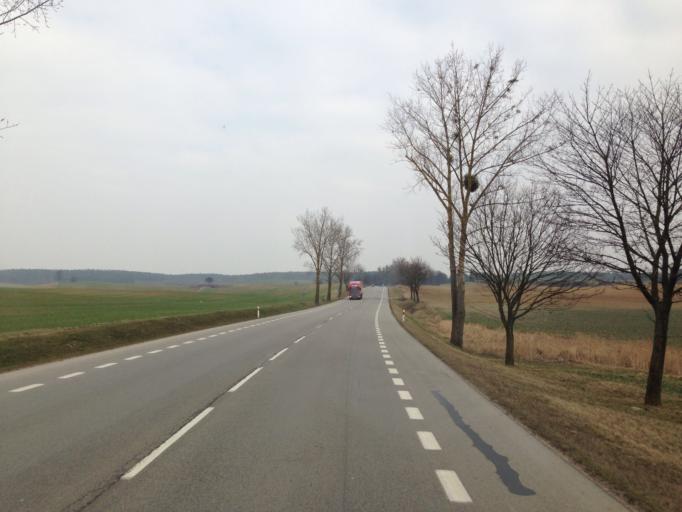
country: PL
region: Pomeranian Voivodeship
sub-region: Powiat tczewski
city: Gniew
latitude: 53.8094
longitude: 18.7830
